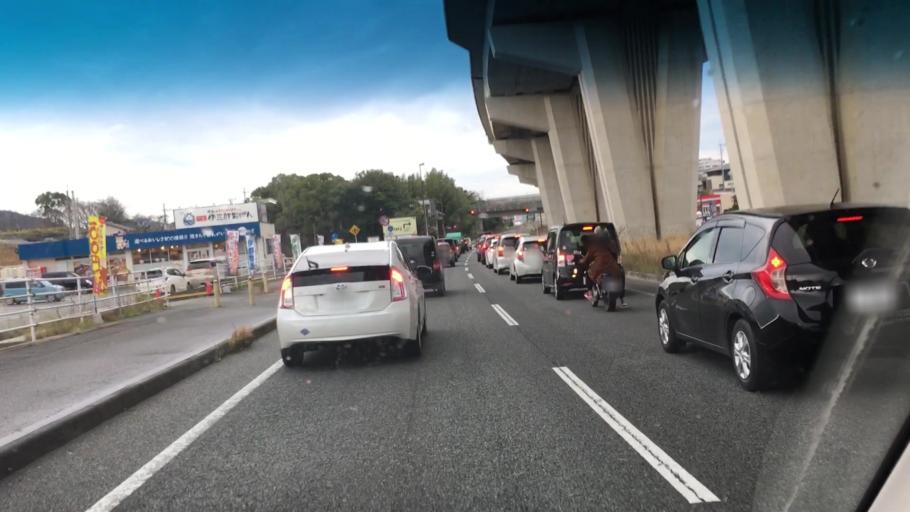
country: JP
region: Fukuoka
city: Maebaru-chuo
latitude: 33.5726
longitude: 130.2689
